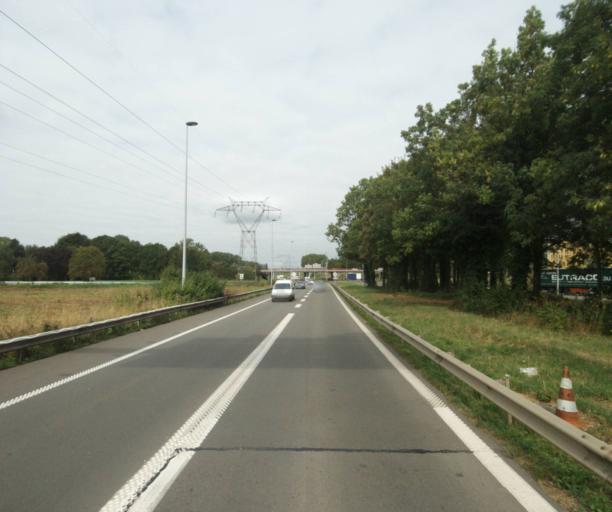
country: FR
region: Nord-Pas-de-Calais
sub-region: Departement du Nord
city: Lesquin
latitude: 50.5988
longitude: 3.1379
